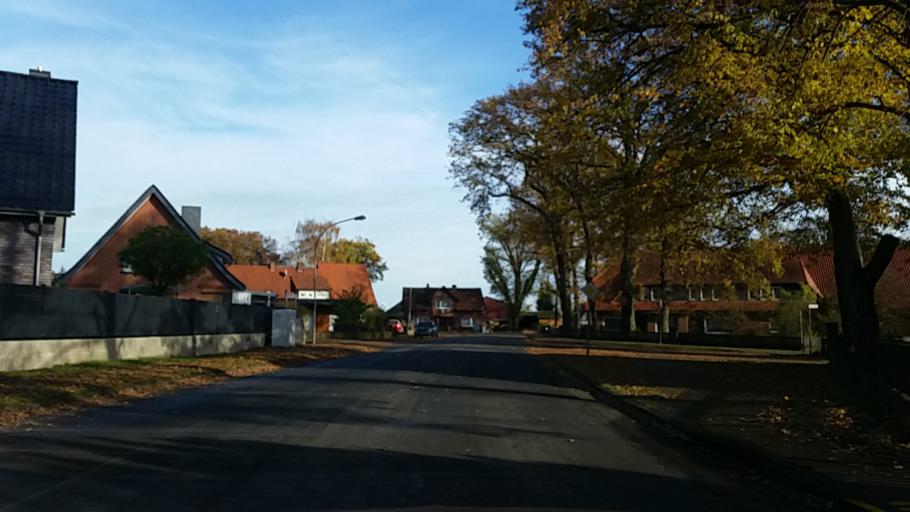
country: DE
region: Lower Saxony
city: Gross Oesingen
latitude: 52.6495
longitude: 10.4659
